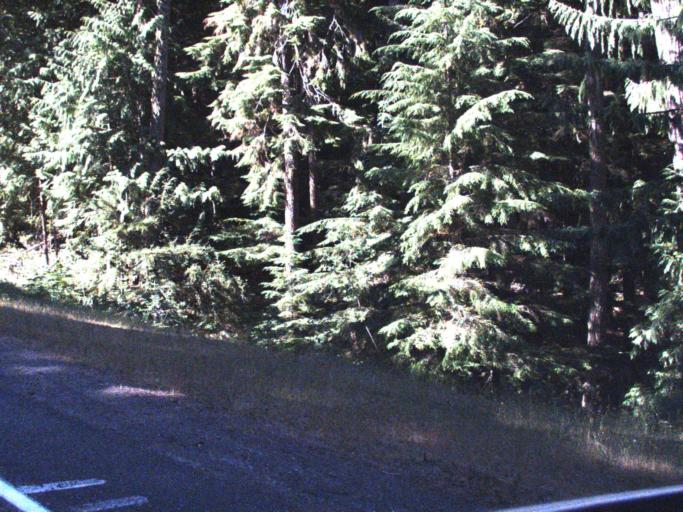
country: US
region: Washington
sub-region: King County
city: Enumclaw
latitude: 47.0121
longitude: -121.5273
